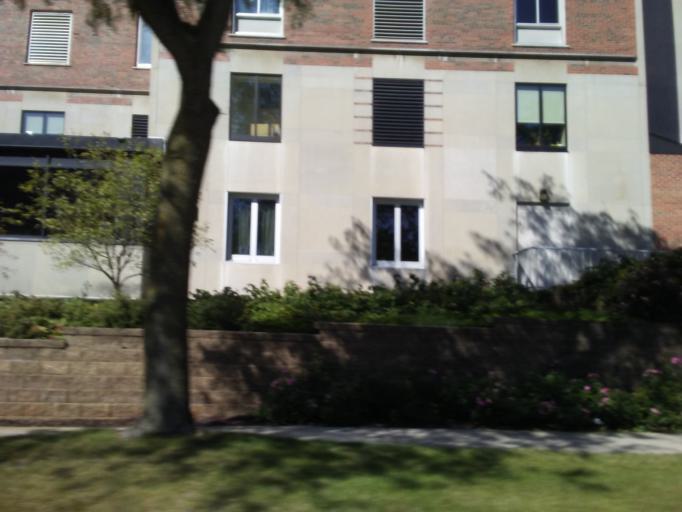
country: US
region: Wisconsin
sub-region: Dane County
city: Madison
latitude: 43.0650
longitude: -89.4010
